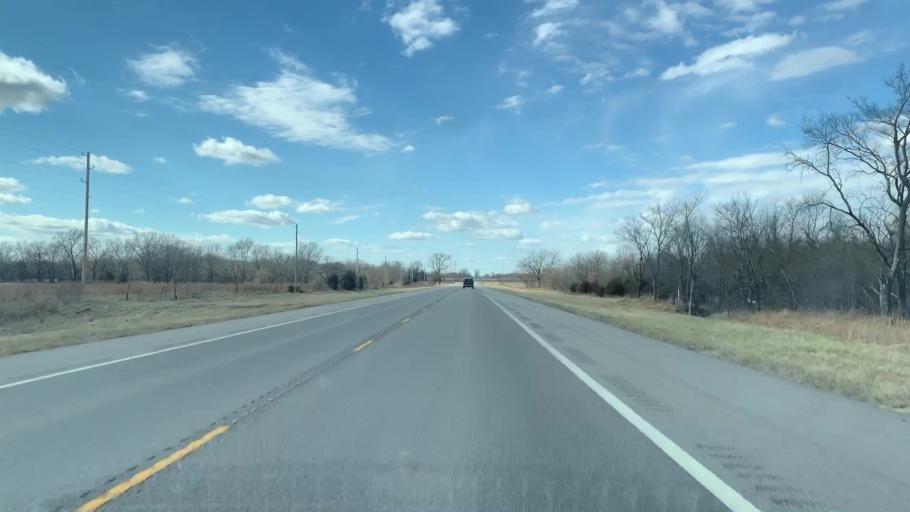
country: US
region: Kansas
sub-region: Labette County
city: Oswego
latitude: 37.3400
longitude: -95.0695
